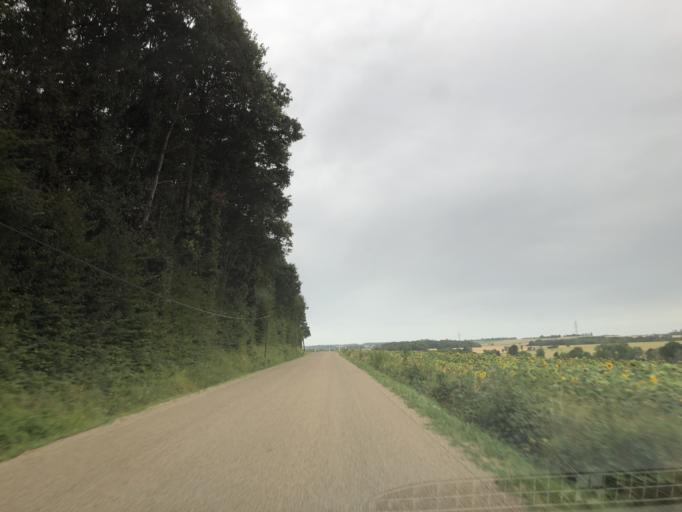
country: FR
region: Bourgogne
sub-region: Departement de l'Yonne
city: Charny
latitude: 47.9597
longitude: 3.1395
